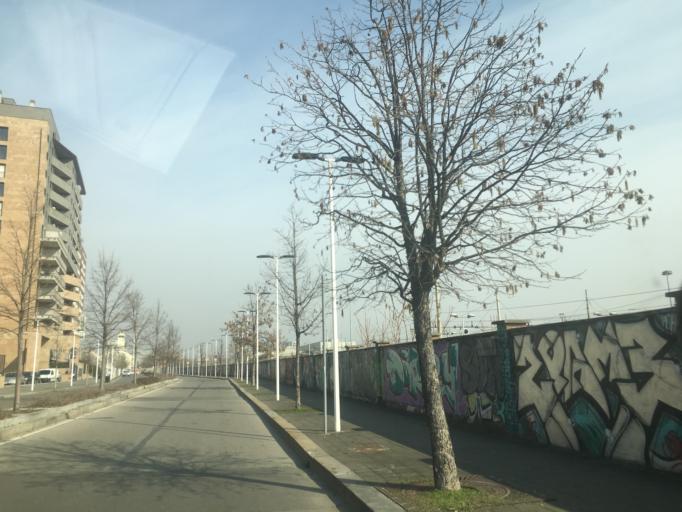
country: IT
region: Lombardy
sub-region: Citta metropolitana di Milano
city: Sesto San Giovanni
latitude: 45.5142
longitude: 9.2149
